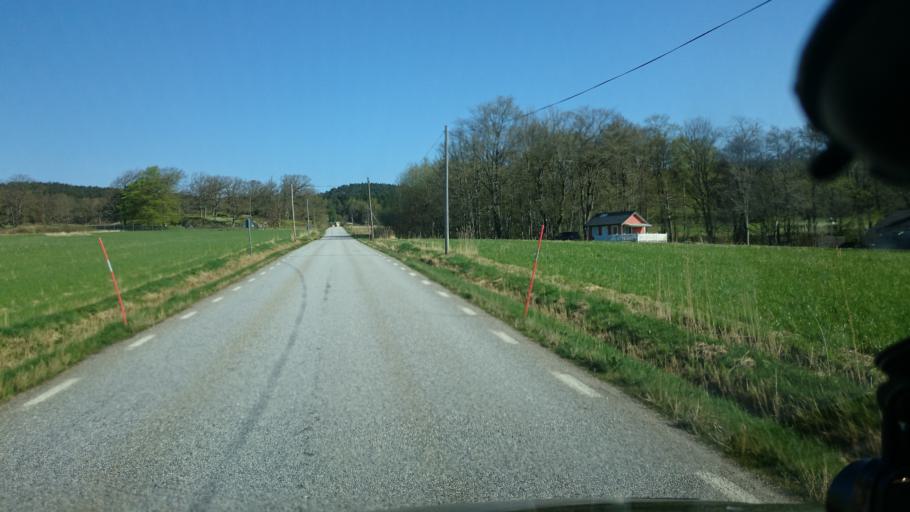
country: SE
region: Vaestra Goetaland
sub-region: Munkedals Kommun
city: Munkedal
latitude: 58.3933
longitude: 11.6534
